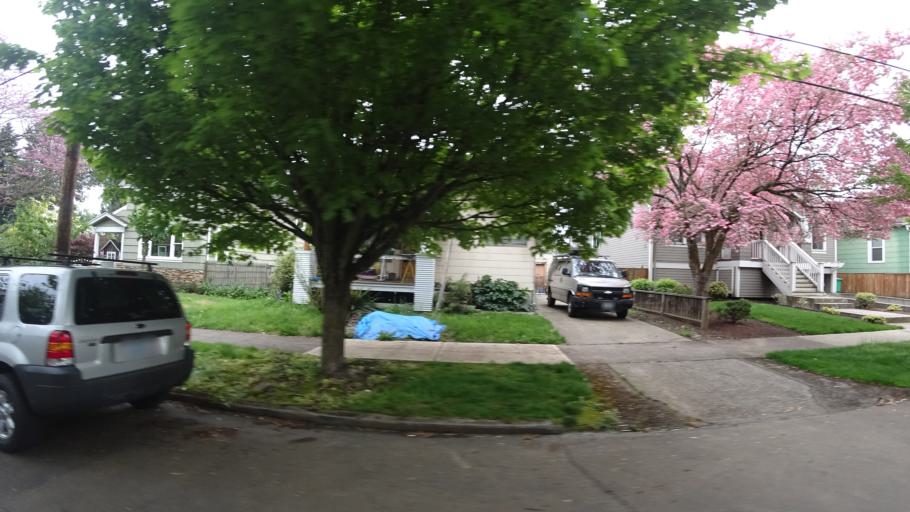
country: US
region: Oregon
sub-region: Clackamas County
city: Milwaukie
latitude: 45.4831
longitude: -122.6459
